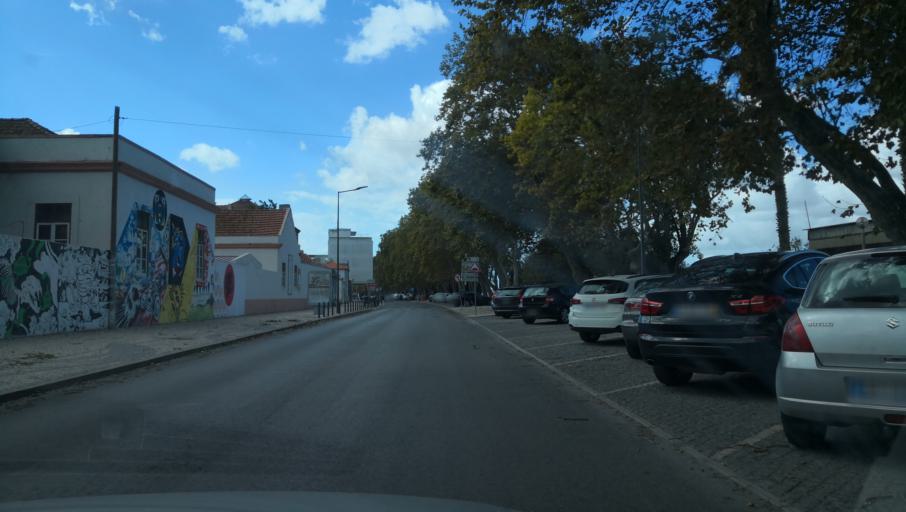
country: PT
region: Setubal
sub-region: Barreiro
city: Barreiro
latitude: 38.6651
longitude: -9.0761
